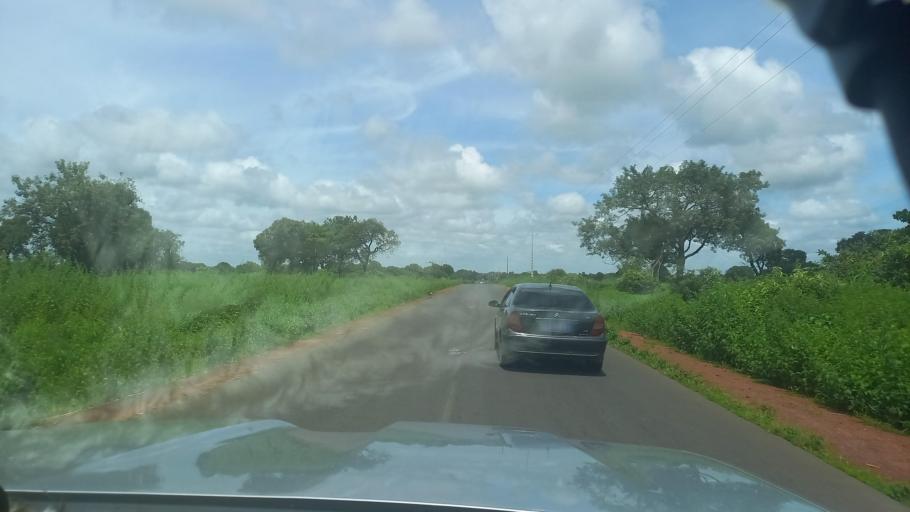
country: GM
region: Lower River
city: Kaiaf
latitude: 13.1952
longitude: -15.5540
